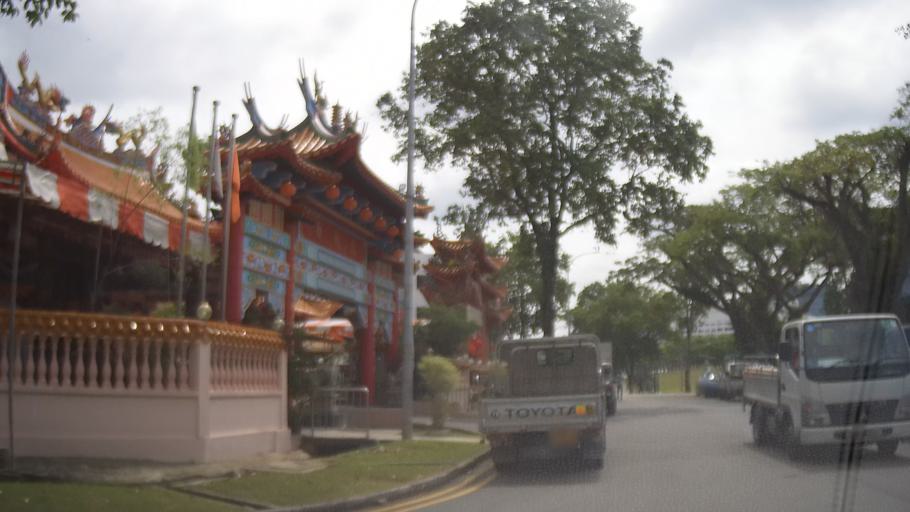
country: MY
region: Johor
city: Johor Bahru
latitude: 1.4396
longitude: 103.7824
